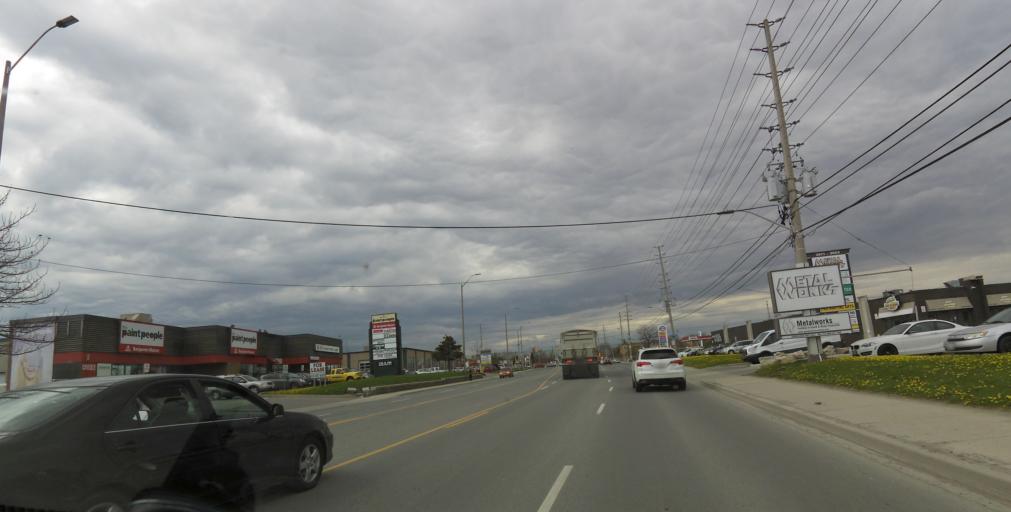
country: CA
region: Ontario
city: Mississauga
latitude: 43.5781
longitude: -79.6498
